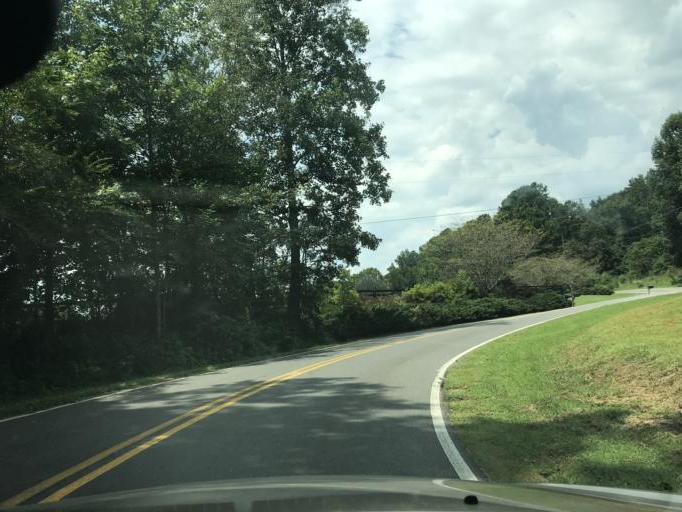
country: US
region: Georgia
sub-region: Dawson County
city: Dawsonville
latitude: 34.3310
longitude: -84.1989
